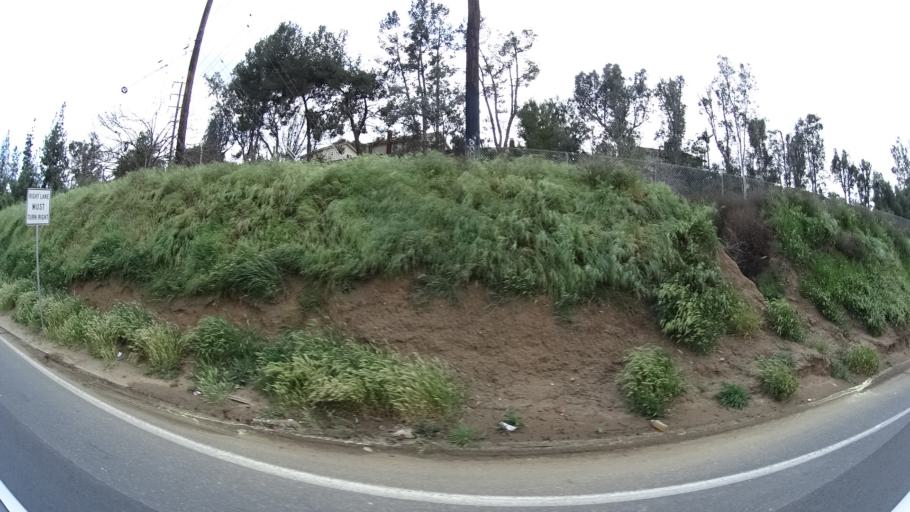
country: US
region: California
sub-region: Los Angeles County
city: Pomona
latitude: 34.0443
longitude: -117.7717
